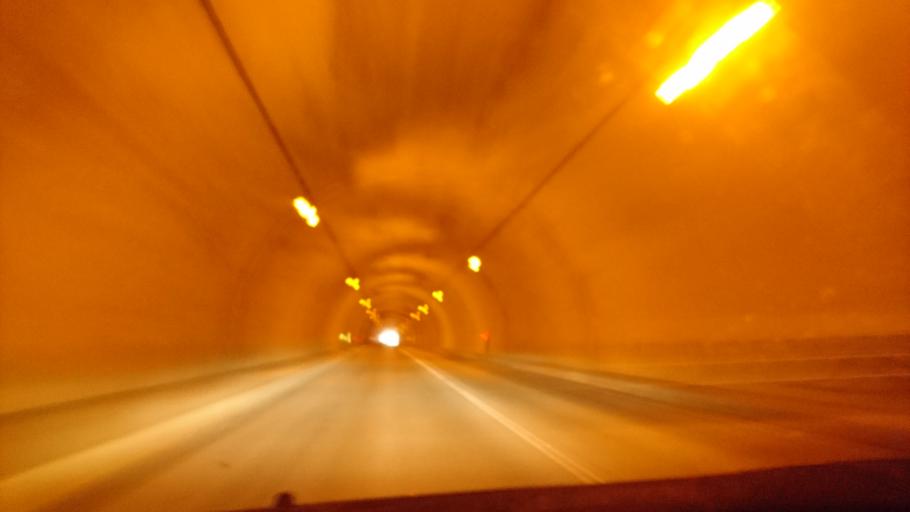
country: JP
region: Iwate
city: Ichinoseki
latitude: 38.8995
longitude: 140.9146
